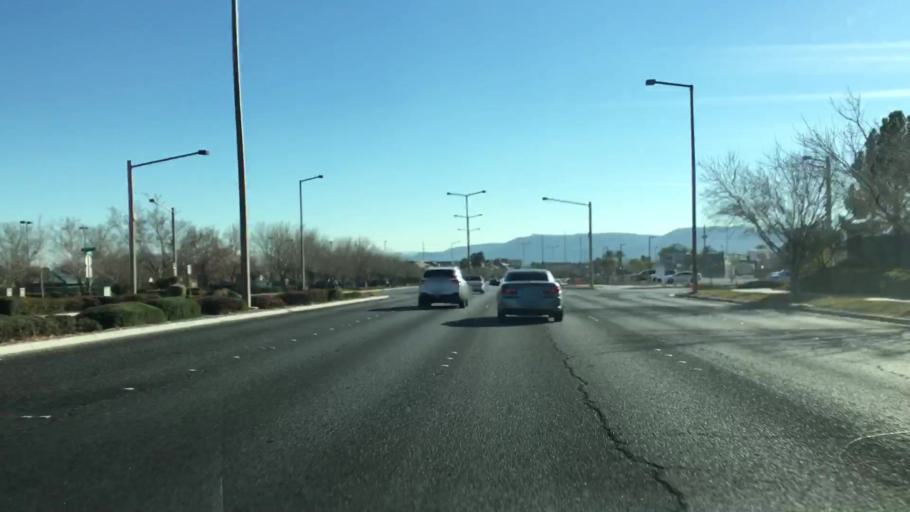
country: US
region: Nevada
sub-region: Clark County
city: Summerlin South
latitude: 36.1277
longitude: -115.3246
